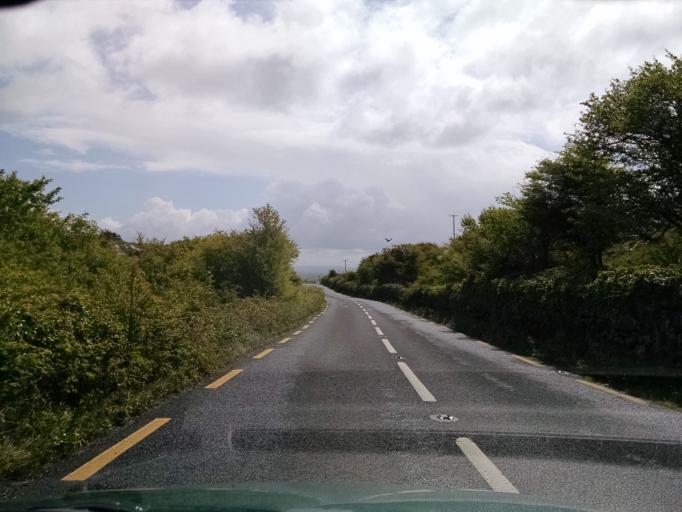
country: IE
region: Connaught
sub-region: County Galway
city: Gaillimh
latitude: 53.1506
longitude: -9.0603
